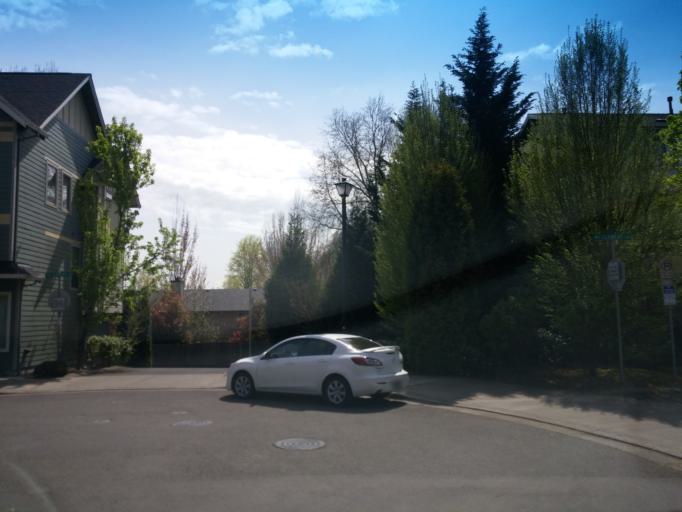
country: US
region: Oregon
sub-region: Washington County
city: Cedar Mill
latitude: 45.5239
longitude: -122.8096
